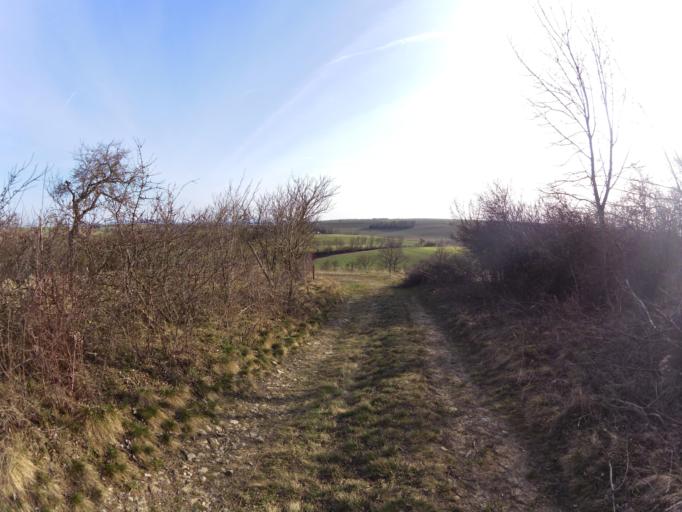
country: DE
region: Bavaria
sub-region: Regierungsbezirk Unterfranken
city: Dettelbach
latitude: 49.8244
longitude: 10.1468
